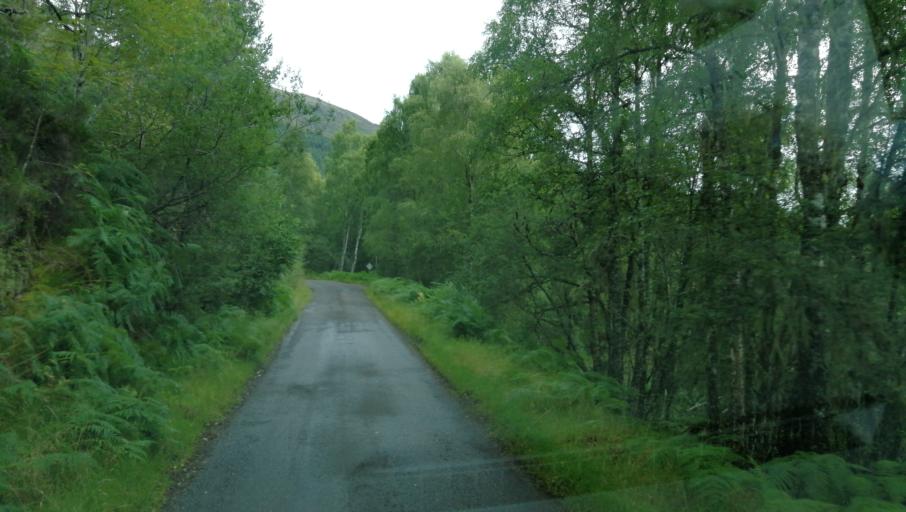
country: GB
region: Scotland
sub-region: Highland
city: Spean Bridge
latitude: 57.3088
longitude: -4.8660
